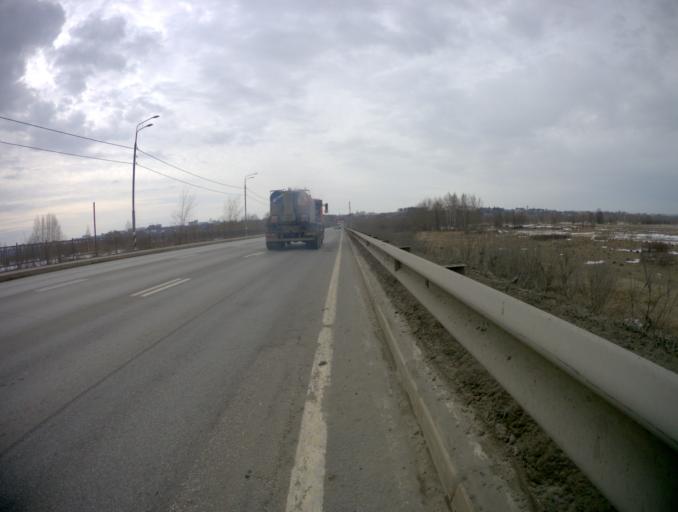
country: RU
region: Vladimir
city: Kommunar
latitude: 56.1154
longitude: 40.4209
